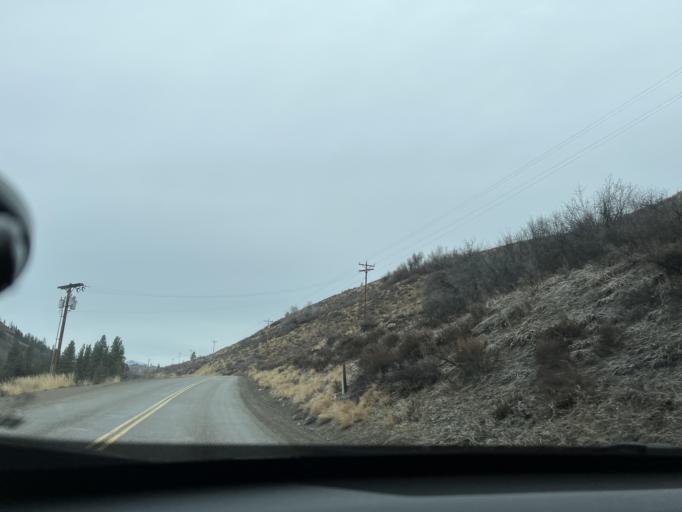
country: US
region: Washington
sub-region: Chelan County
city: Granite Falls
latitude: 48.4492
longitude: -120.2389
